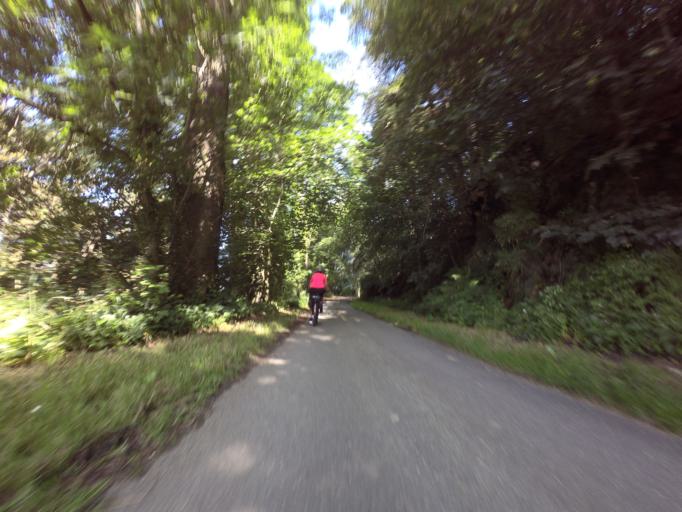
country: GB
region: Scotland
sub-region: Aberdeenshire
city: Banff
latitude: 57.6117
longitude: -2.5114
